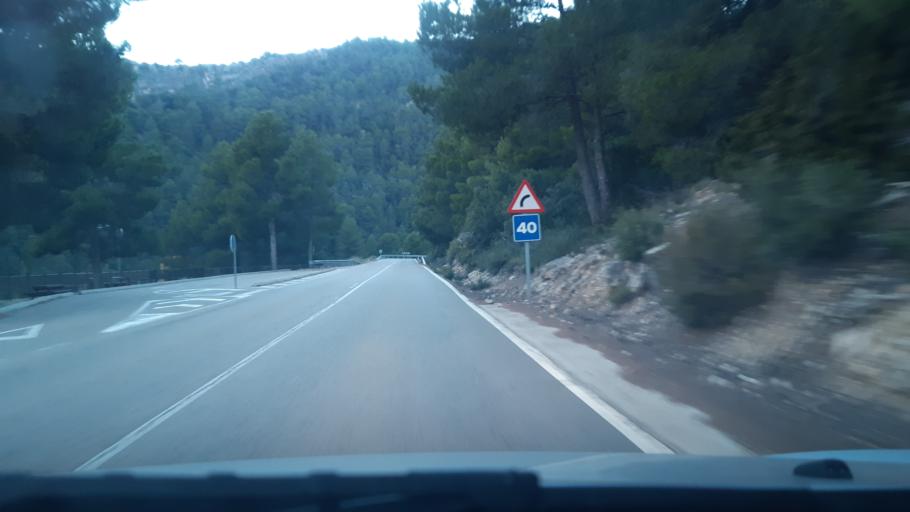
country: ES
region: Aragon
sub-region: Provincia de Teruel
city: Valderrobres
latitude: 40.8414
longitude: 0.1785
